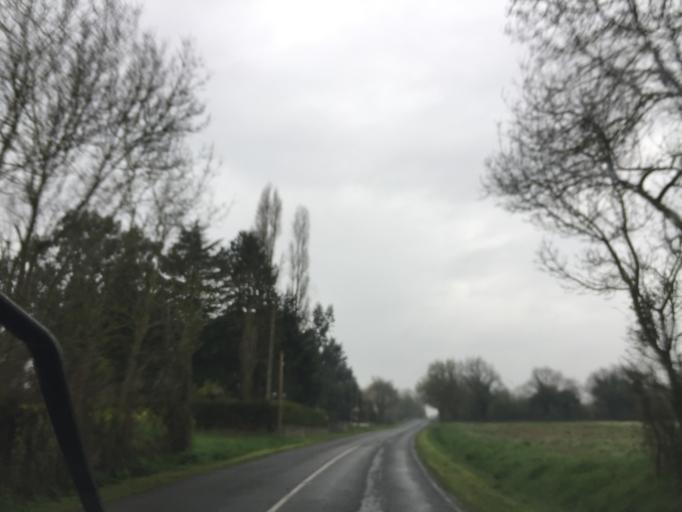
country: FR
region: Pays de la Loire
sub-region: Departement de la Loire-Atlantique
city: Suce-sur-Erdre
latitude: 47.3620
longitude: -1.5271
